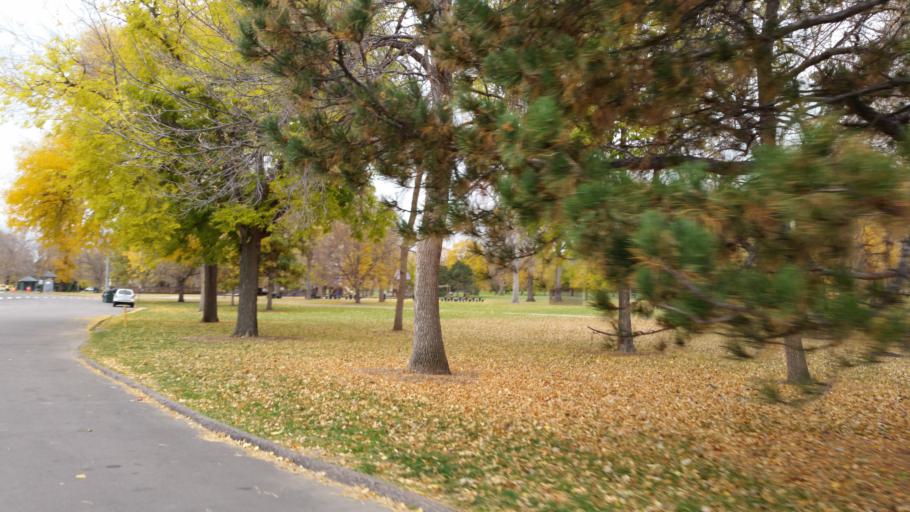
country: US
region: Colorado
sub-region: Denver County
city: Denver
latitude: 39.7490
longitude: -104.9550
